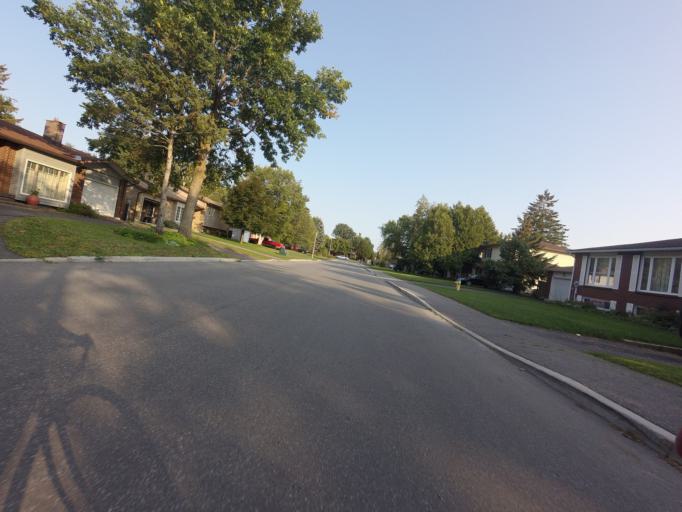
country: CA
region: Ontario
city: Bells Corners
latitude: 45.2949
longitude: -75.8834
